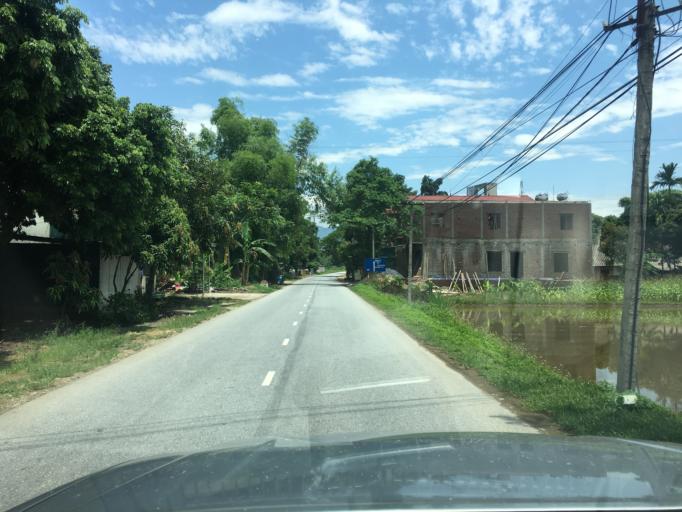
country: VN
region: Yen Bai
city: Son Thinh
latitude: 21.6353
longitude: 104.5036
